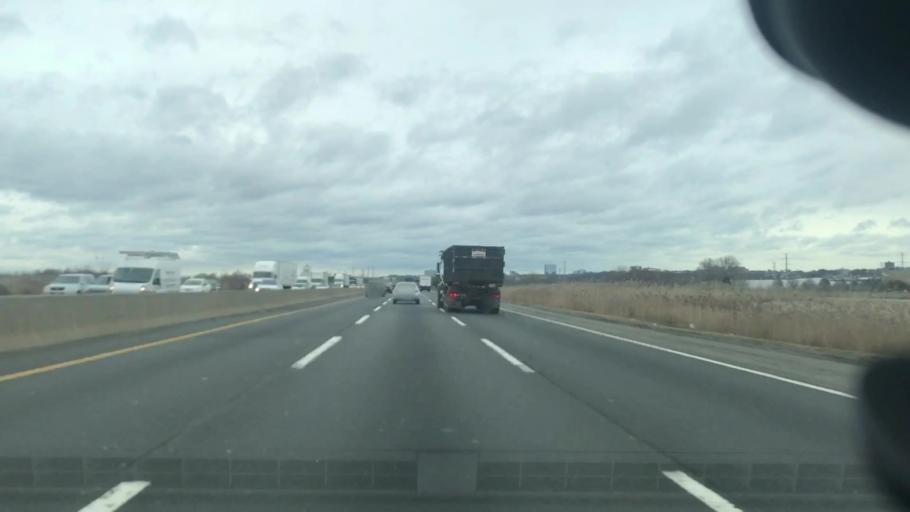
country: US
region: New Jersey
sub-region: Hudson County
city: Secaucus
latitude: 40.7970
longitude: -74.0405
